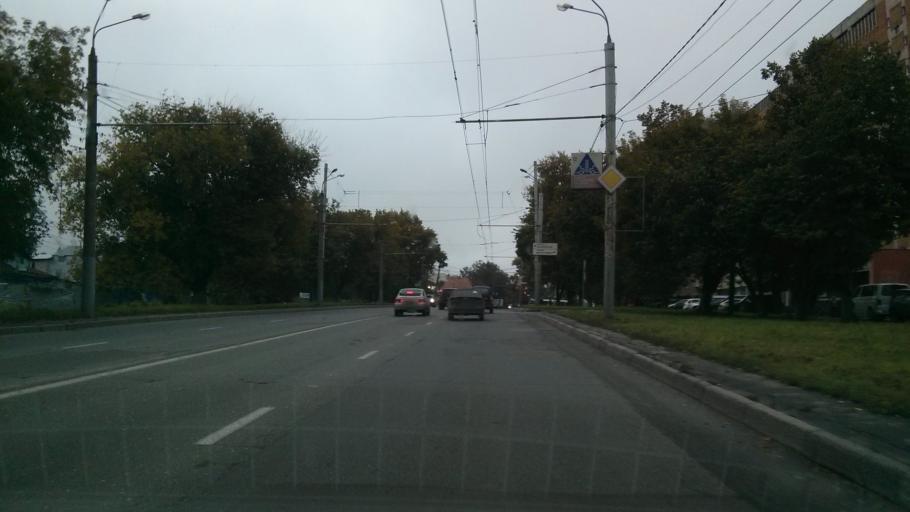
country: RU
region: Nizjnij Novgorod
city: Bor
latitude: 56.3202
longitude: 44.0522
